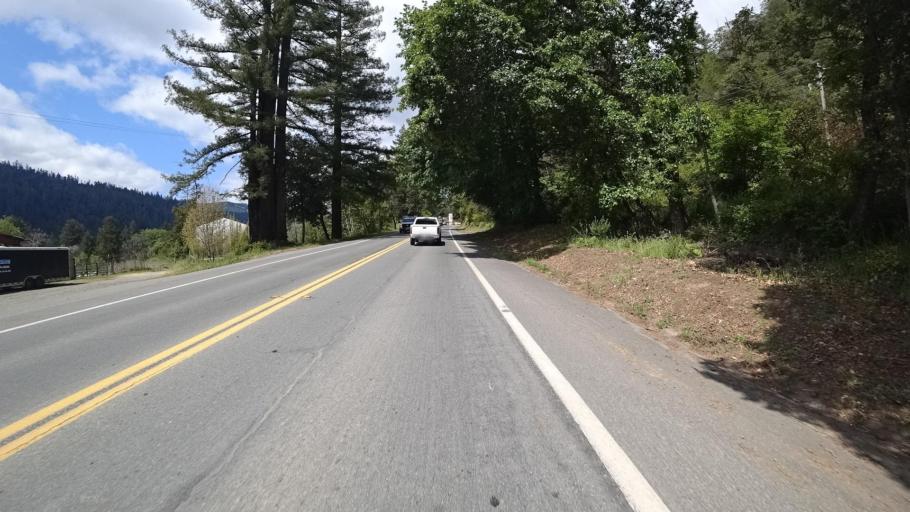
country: US
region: California
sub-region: Humboldt County
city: Redway
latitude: 40.1161
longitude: -123.8165
